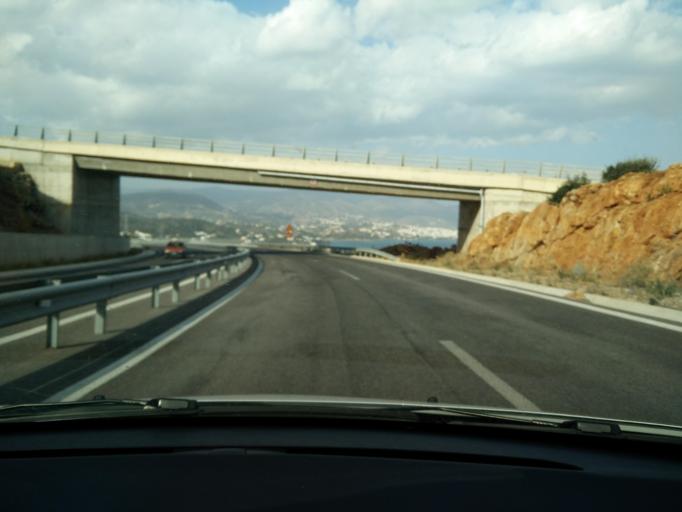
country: GR
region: Crete
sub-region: Nomos Lasithiou
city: Agios Nikolaos
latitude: 35.1550
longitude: 25.7152
